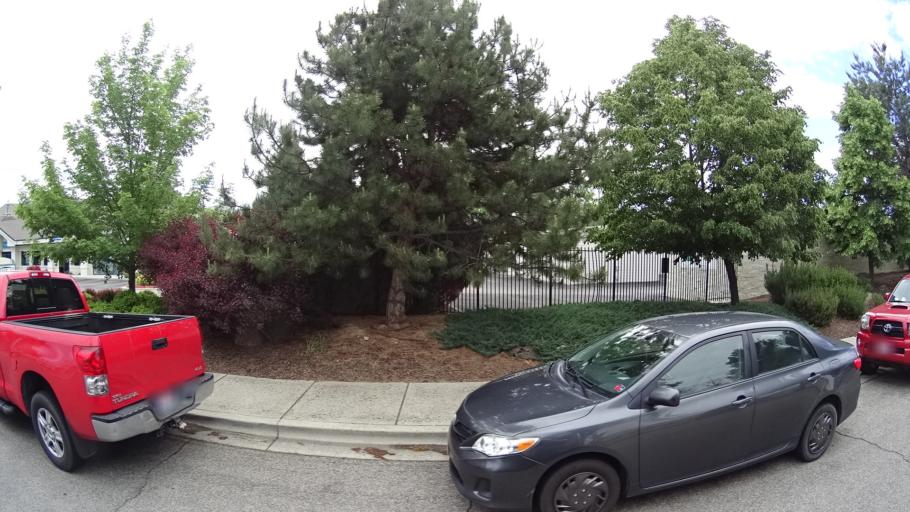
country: US
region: Idaho
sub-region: Ada County
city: Boise
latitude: 43.5814
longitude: -116.1691
